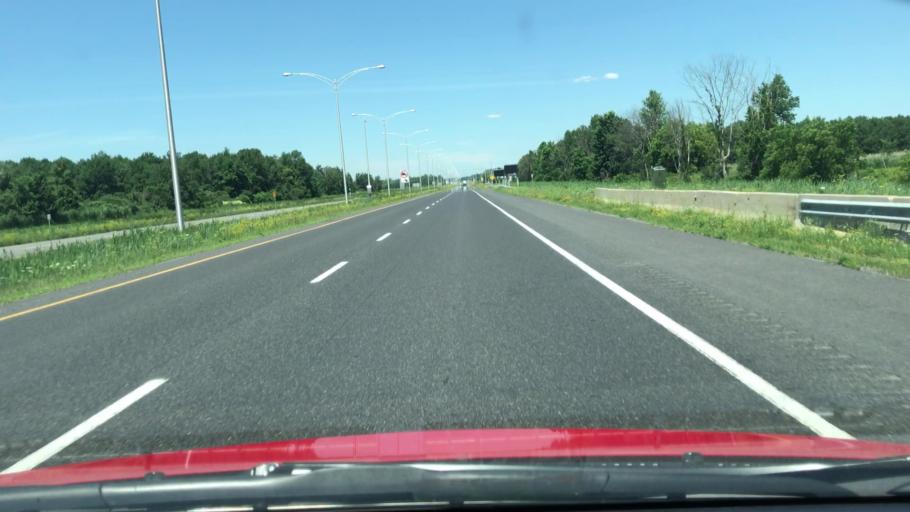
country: US
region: New York
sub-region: Clinton County
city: Champlain
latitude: 45.0275
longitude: -73.4532
